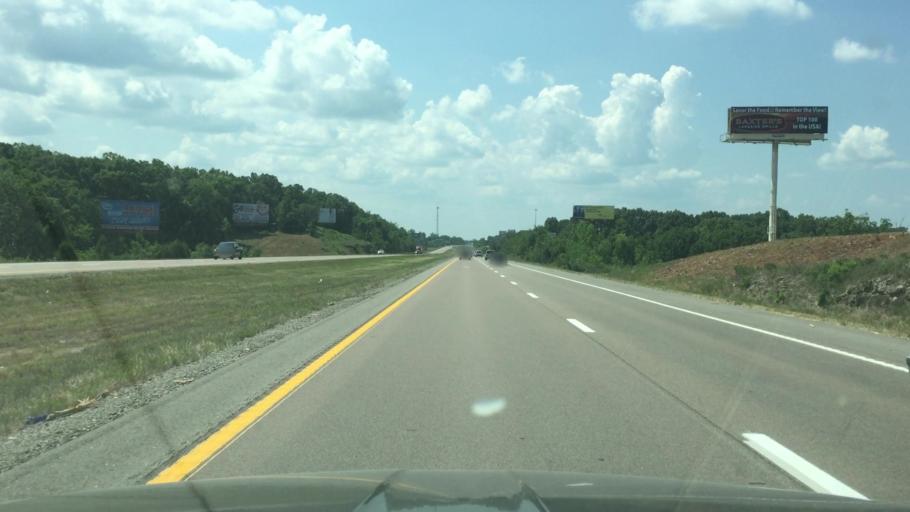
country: US
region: Missouri
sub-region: Miller County
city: Eldon
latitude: 38.2791
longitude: -92.5814
